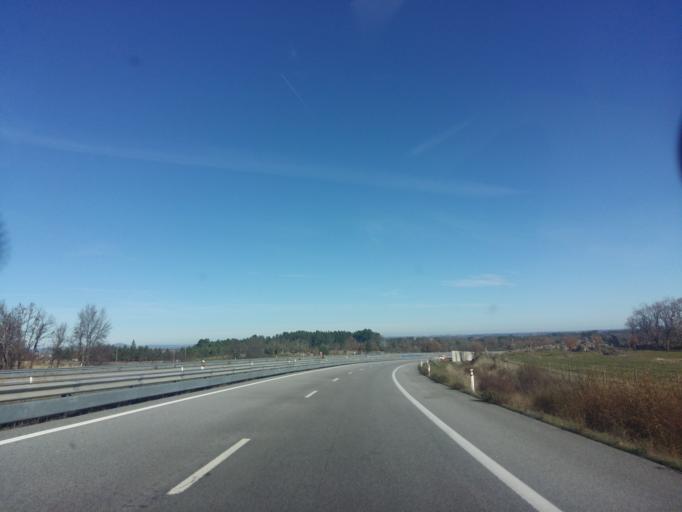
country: PT
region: Guarda
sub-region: Guarda
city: Sequeira
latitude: 40.5988
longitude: -7.1305
